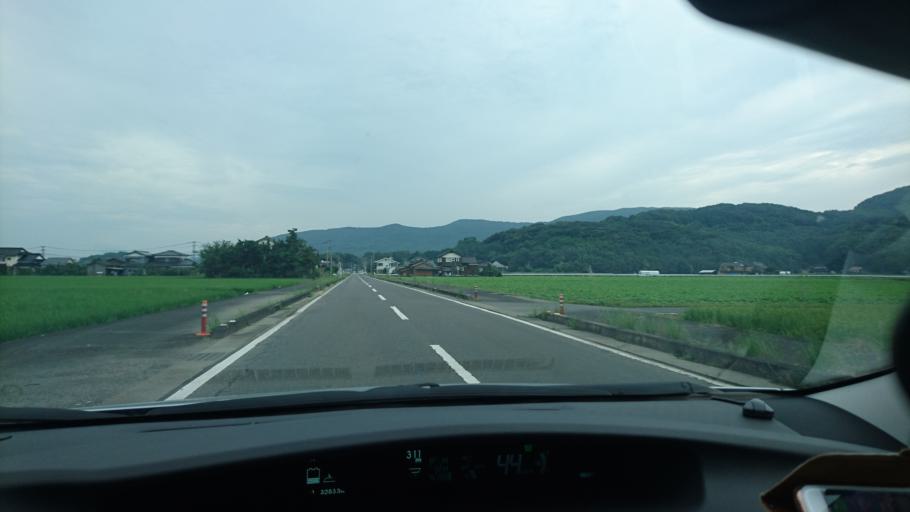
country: JP
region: Saga Prefecture
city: Takeocho-takeo
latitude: 33.1953
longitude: 130.1018
